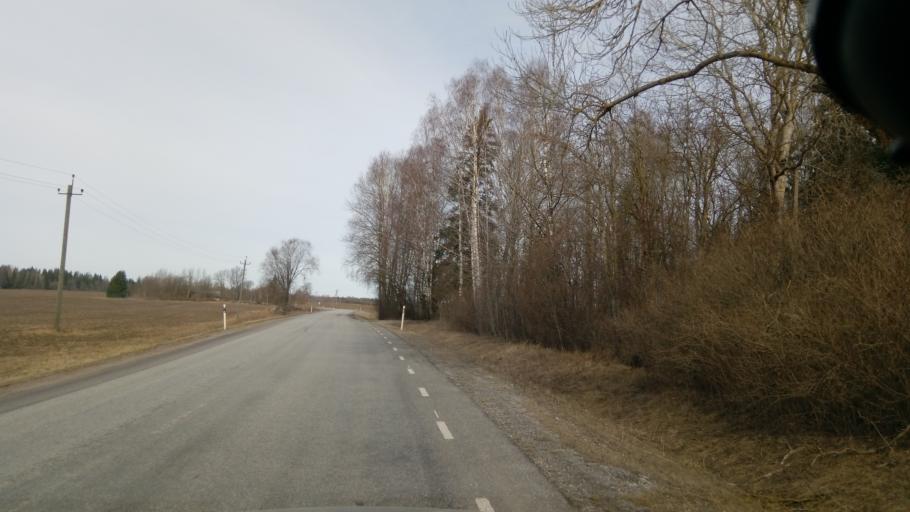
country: EE
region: Raplamaa
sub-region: Rapla vald
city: Rapla
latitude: 59.0259
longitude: 24.8385
